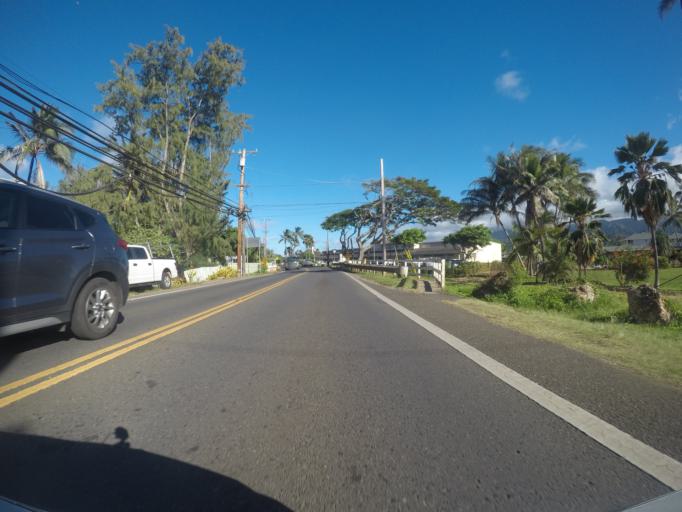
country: US
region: Hawaii
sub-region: Honolulu County
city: La'ie
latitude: 21.6482
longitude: -157.9229
